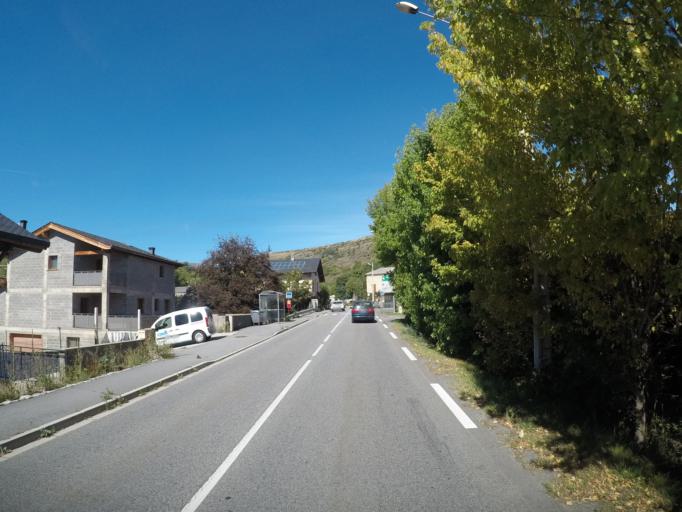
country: FR
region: Languedoc-Roussillon
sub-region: Departement des Pyrenees-Orientales
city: la Guingueta d'Ix
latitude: 42.4608
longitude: 1.9385
